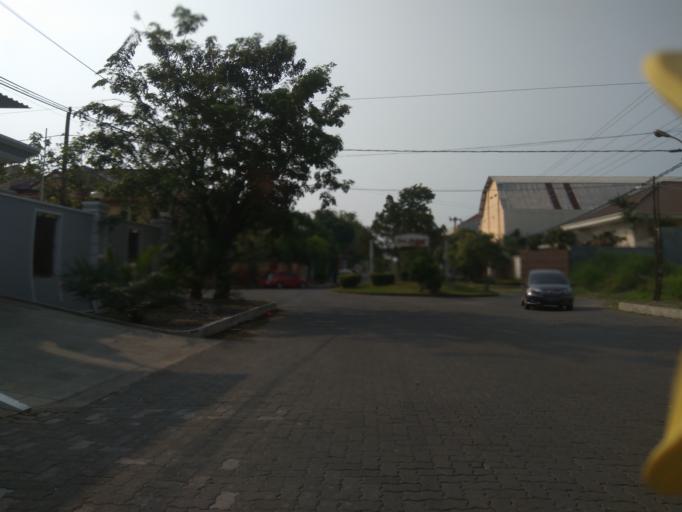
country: ID
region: Central Java
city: Semarang
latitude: -6.9649
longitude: 110.3863
